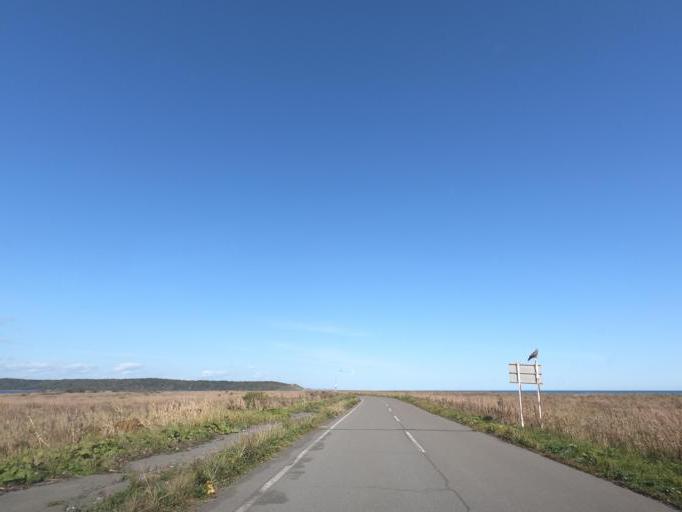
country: JP
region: Hokkaido
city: Obihiro
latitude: 42.5875
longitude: 143.5367
